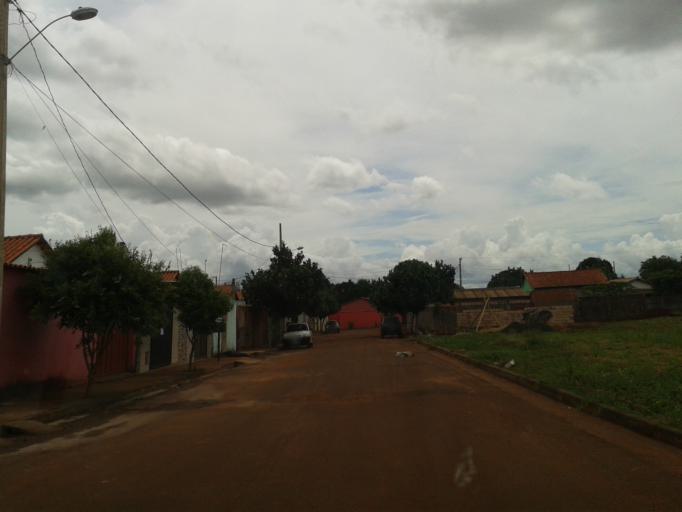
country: BR
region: Minas Gerais
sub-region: Centralina
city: Centralina
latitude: -18.5851
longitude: -49.2060
